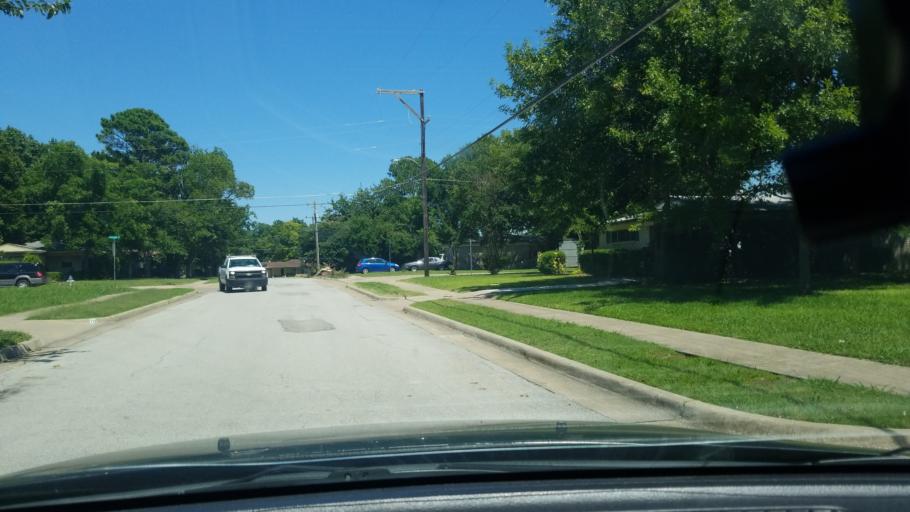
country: US
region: Texas
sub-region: Dallas County
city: Mesquite
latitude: 32.7593
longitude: -96.6004
